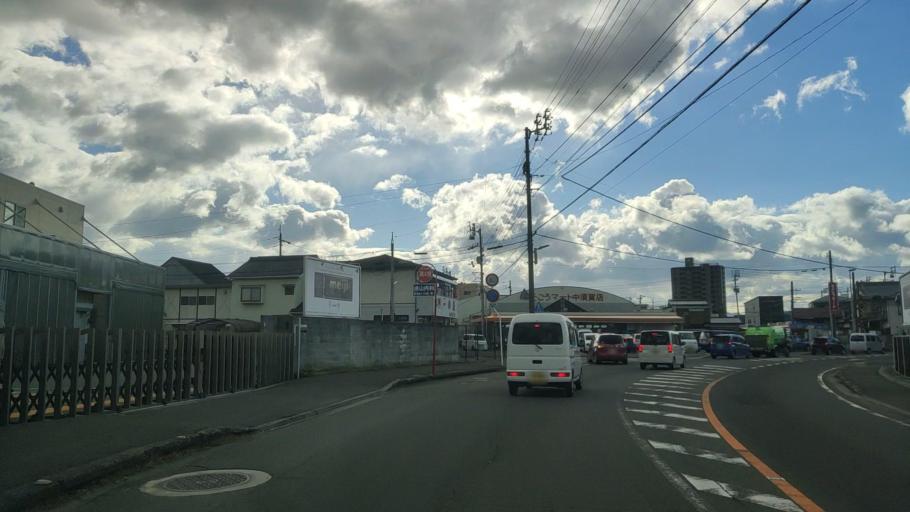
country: JP
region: Ehime
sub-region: Shikoku-chuo Shi
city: Matsuyama
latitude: 33.8660
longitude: 132.7193
